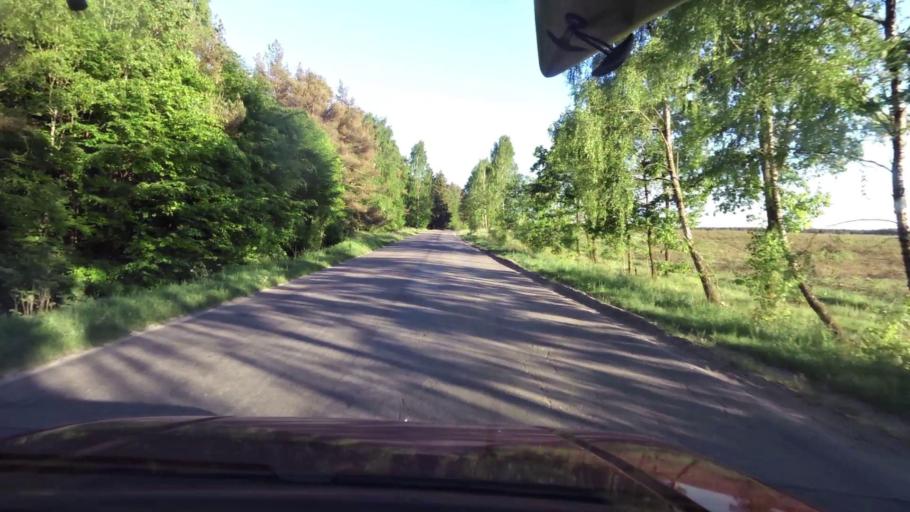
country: PL
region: West Pomeranian Voivodeship
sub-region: Powiat szczecinecki
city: Bialy Bor
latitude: 53.9120
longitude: 16.8083
